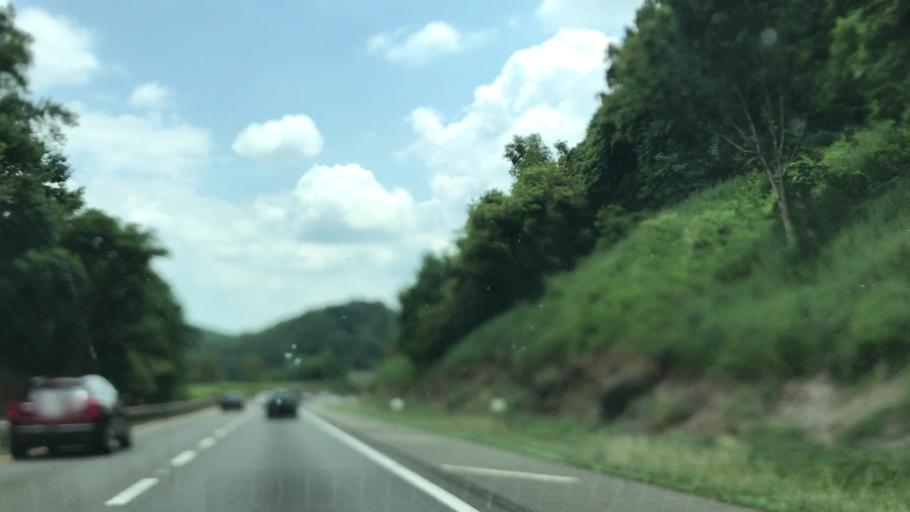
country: US
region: Virginia
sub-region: Carroll County
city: Cana
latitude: 36.6077
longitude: -80.7372
